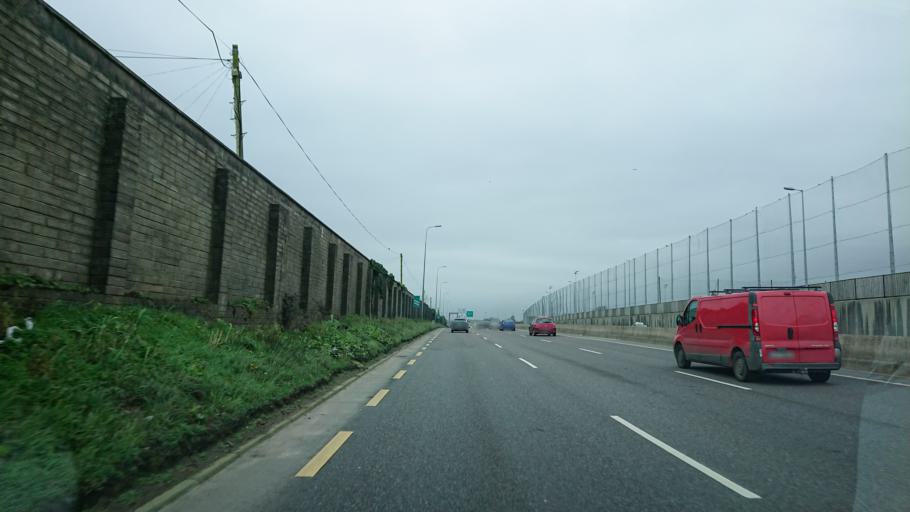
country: IE
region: Munster
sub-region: County Cork
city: Cork
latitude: 51.8759
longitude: -8.4966
